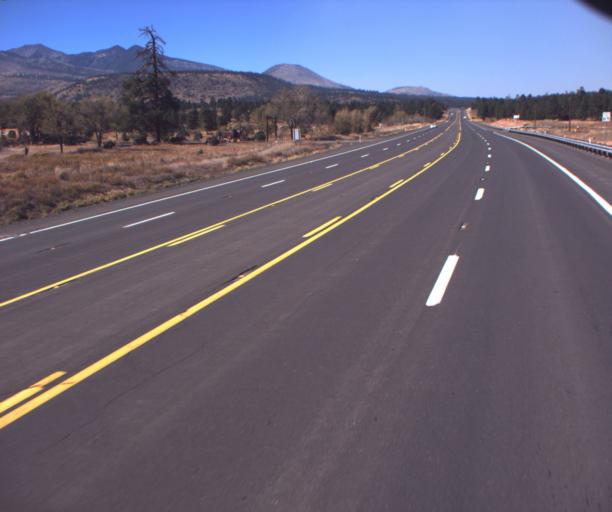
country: US
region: Arizona
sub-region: Coconino County
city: Flagstaff
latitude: 35.3340
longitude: -111.5492
